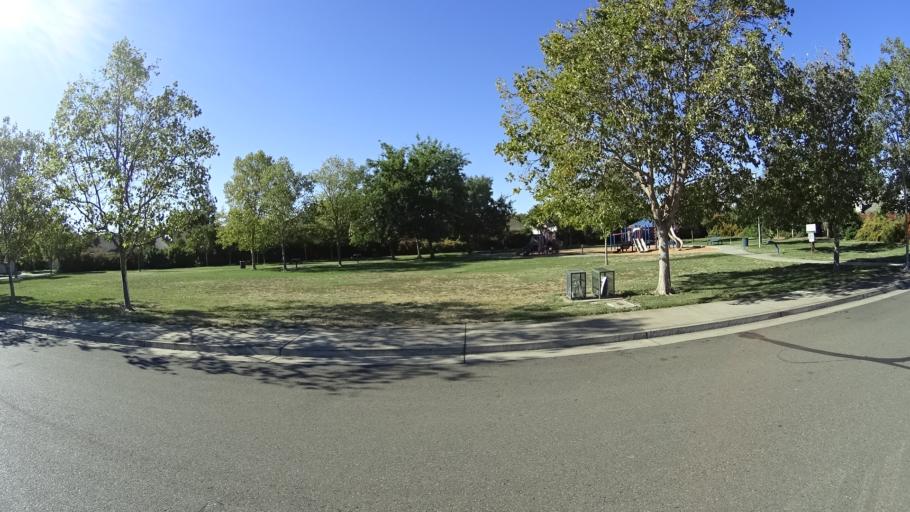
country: US
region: California
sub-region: Sacramento County
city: Vineyard
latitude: 38.4454
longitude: -121.3758
